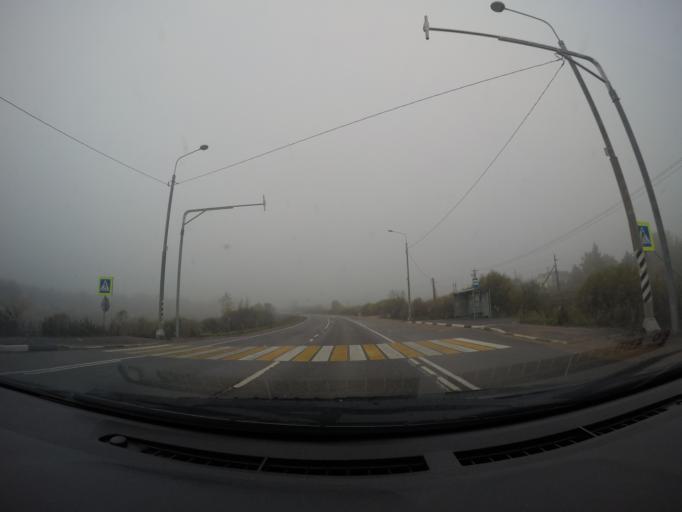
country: RU
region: Moskovskaya
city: Ruza
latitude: 55.7303
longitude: 36.3274
